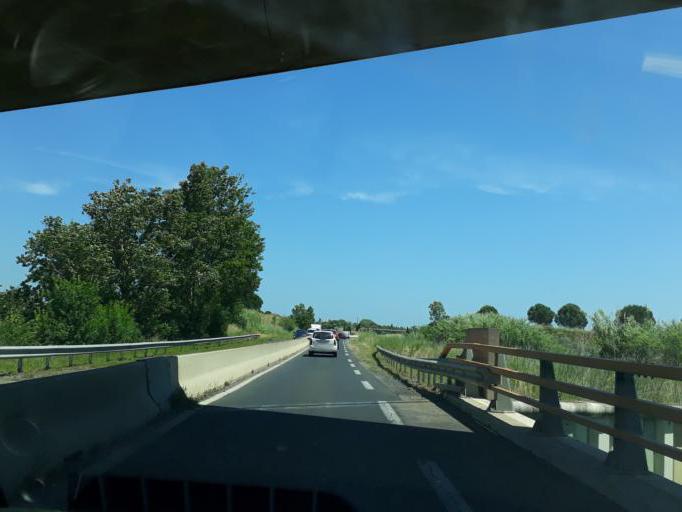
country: FR
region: Languedoc-Roussillon
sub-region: Departement de l'Herault
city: Vias
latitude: 43.3107
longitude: 3.4013
